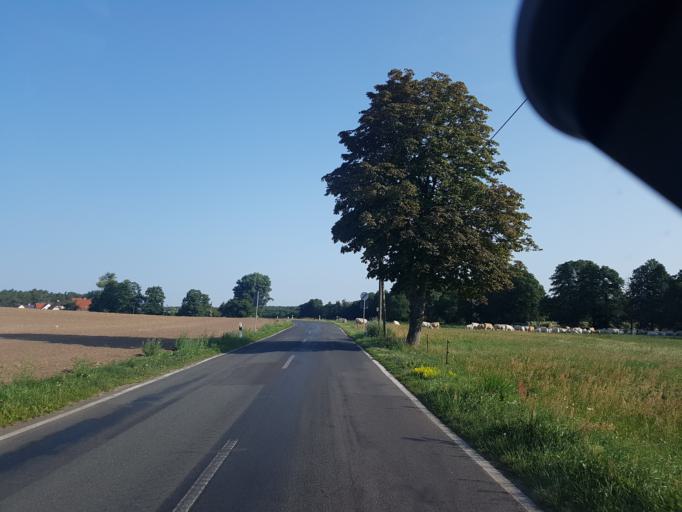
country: DE
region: Brandenburg
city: Niemegk
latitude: 52.1570
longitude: 12.6910
